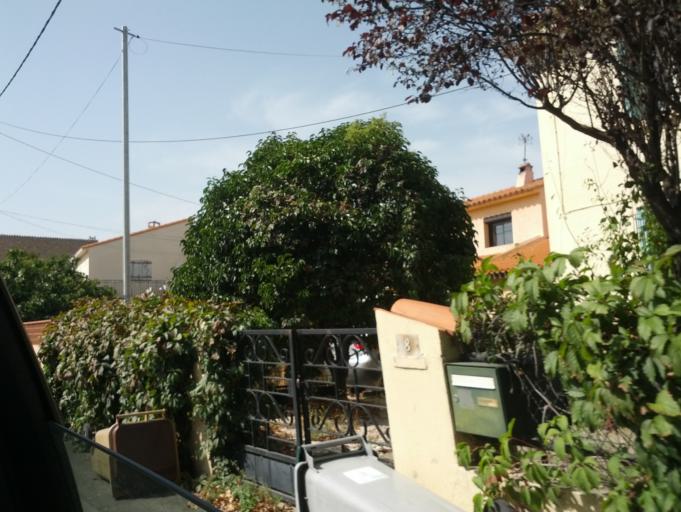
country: FR
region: Languedoc-Roussillon
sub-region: Departement des Pyrenees-Orientales
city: Peyrestortes
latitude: 42.7756
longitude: 2.8350
